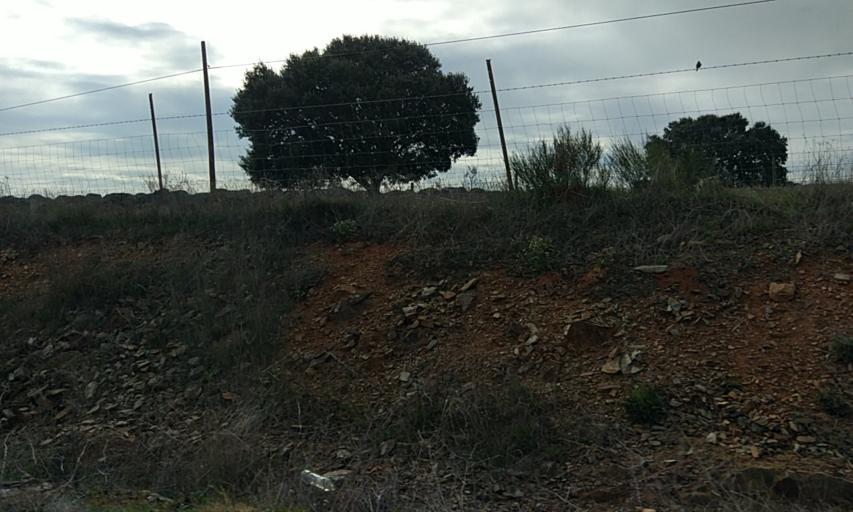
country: ES
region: Castille and Leon
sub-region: Provincia de Salamanca
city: Herguijuela de Ciudad Rodrigo
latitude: 40.4676
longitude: -6.5842
